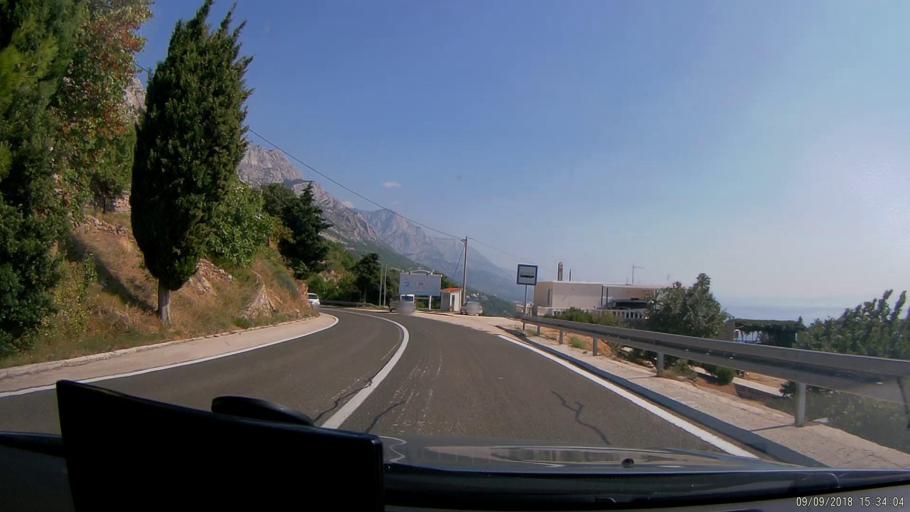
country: HR
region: Splitsko-Dalmatinska
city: Donja Brela
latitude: 43.3895
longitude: 16.9017
